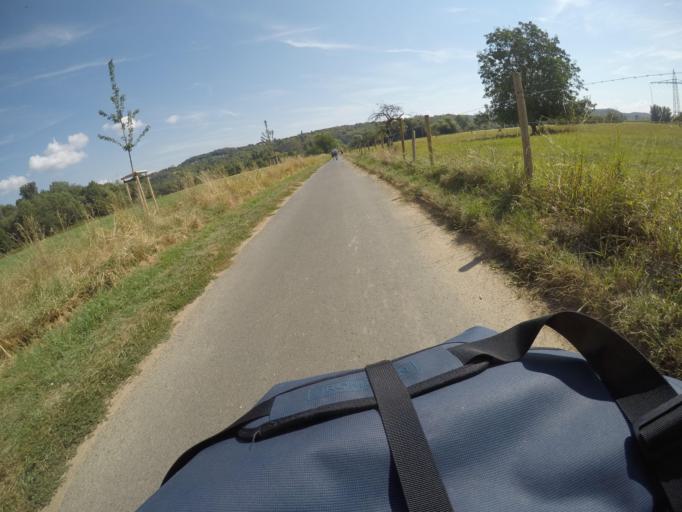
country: DE
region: Rheinland-Pfalz
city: Linz am Rhein
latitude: 50.5529
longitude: 7.2703
